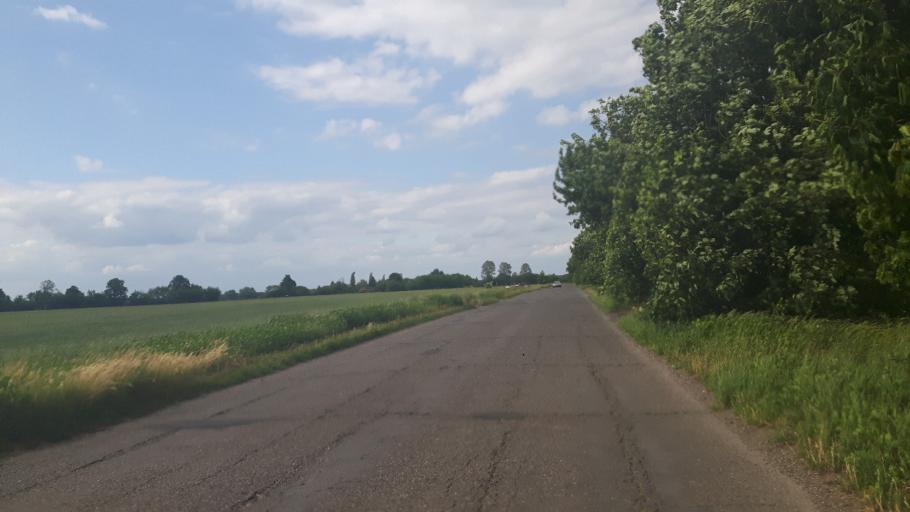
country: DE
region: Brandenburg
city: Rudnitz
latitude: 52.6899
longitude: 13.6584
